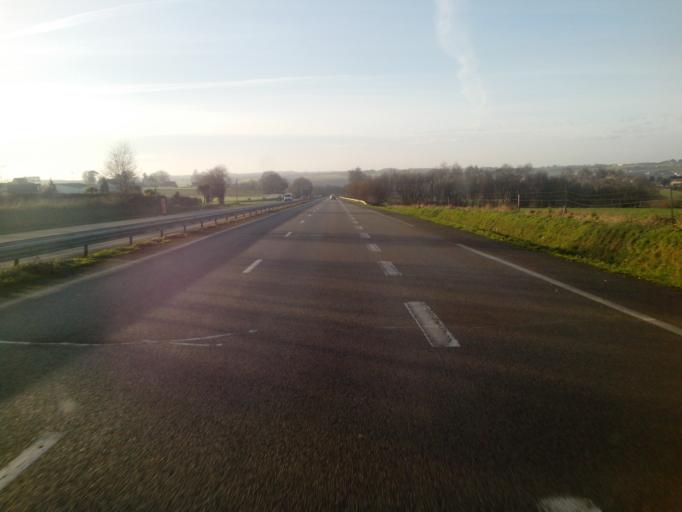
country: FR
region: Brittany
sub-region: Departement du Morbihan
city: Guenin
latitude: 47.8962
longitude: -2.9438
